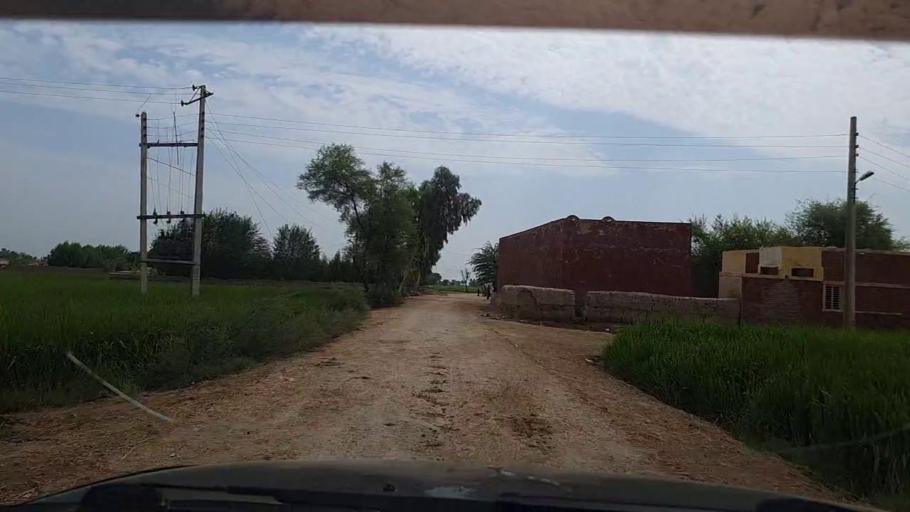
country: PK
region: Sindh
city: Thul
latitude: 28.2409
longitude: 68.7229
